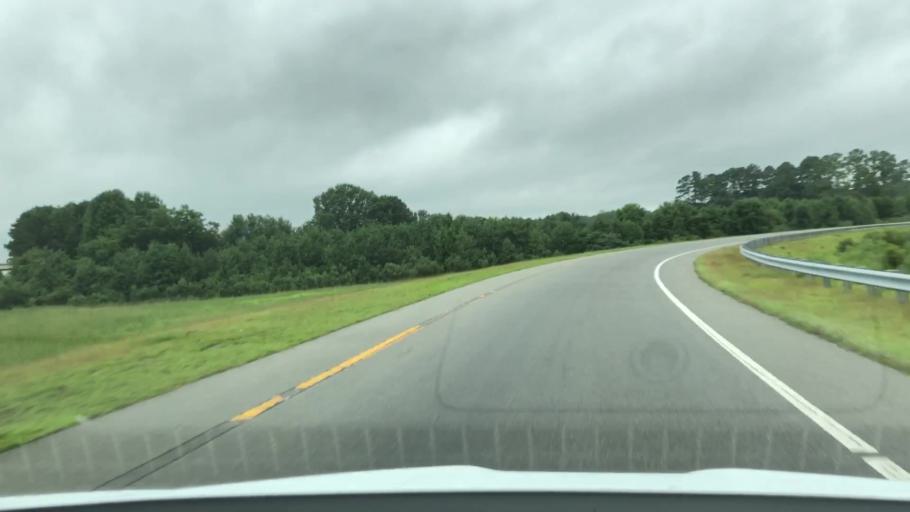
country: US
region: North Carolina
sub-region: Wayne County
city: Goldsboro
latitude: 35.4274
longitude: -77.9885
